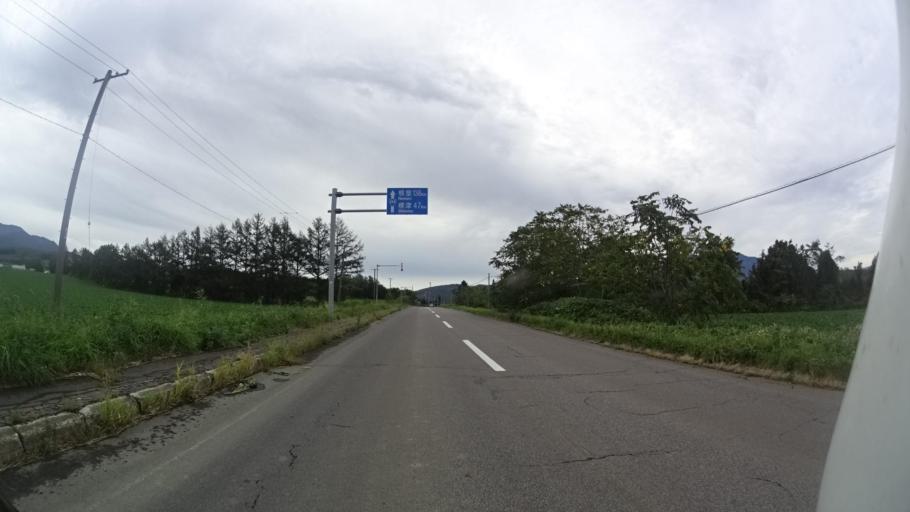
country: JP
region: Hokkaido
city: Shibetsu
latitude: 43.8734
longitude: 144.7473
